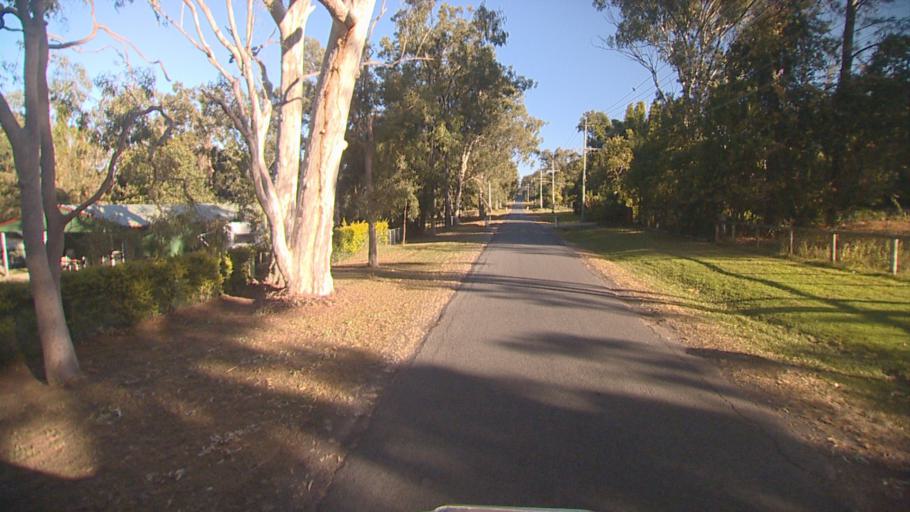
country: AU
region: Queensland
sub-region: Logan
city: Chambers Flat
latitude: -27.7804
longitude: 153.0874
